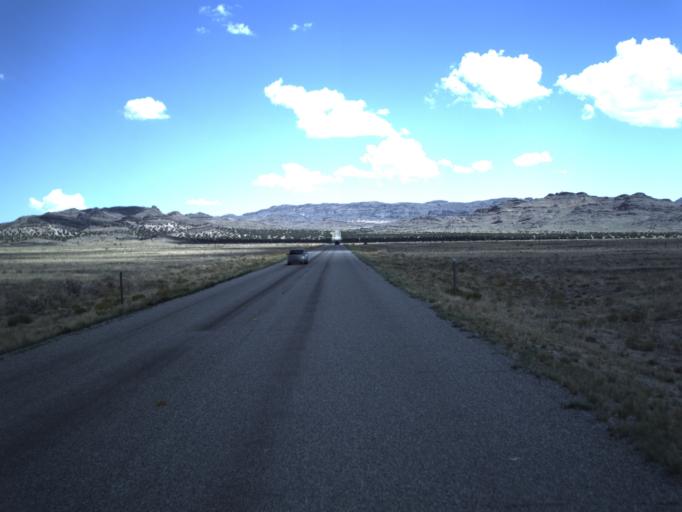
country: US
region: Utah
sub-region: Beaver County
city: Milford
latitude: 39.0628
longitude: -113.7494
